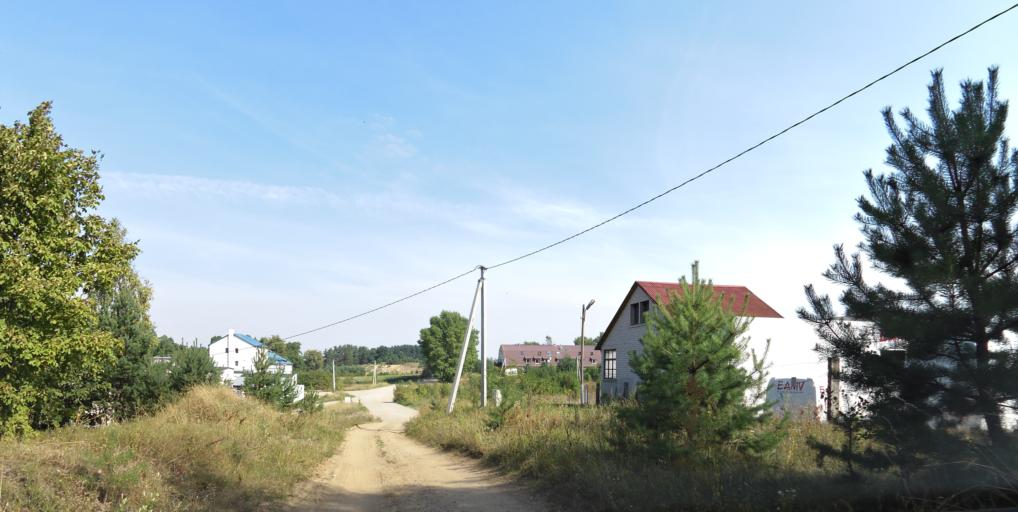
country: LT
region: Vilnius County
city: Pilaite
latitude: 54.7016
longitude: 25.1964
